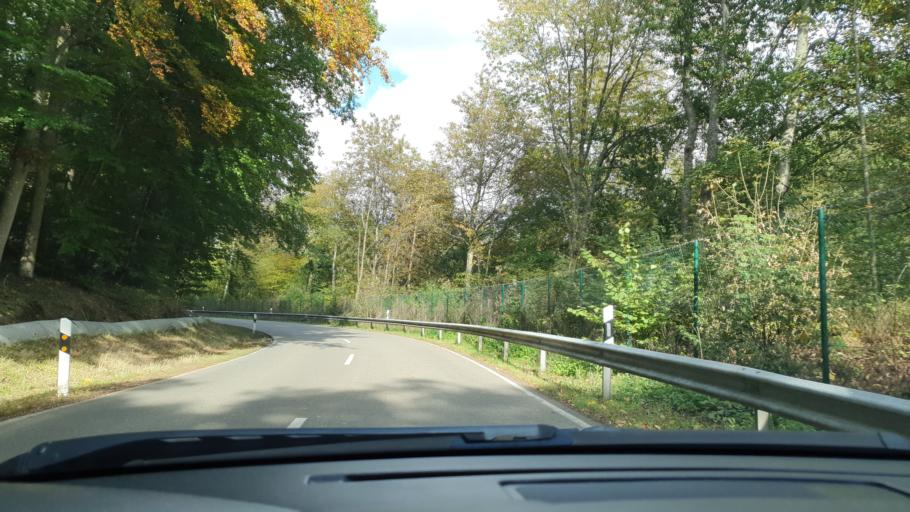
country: DE
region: Rheinland-Pfalz
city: Kaiserslautern
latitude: 49.4281
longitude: 7.8185
